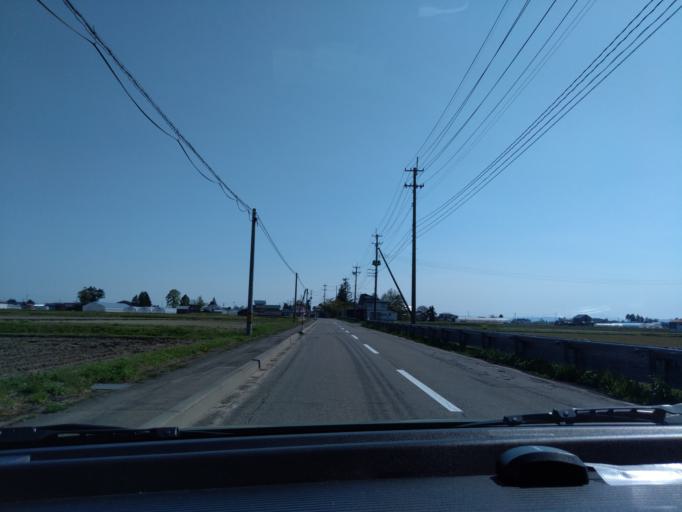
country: JP
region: Akita
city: Omagari
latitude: 39.4474
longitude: 140.5679
